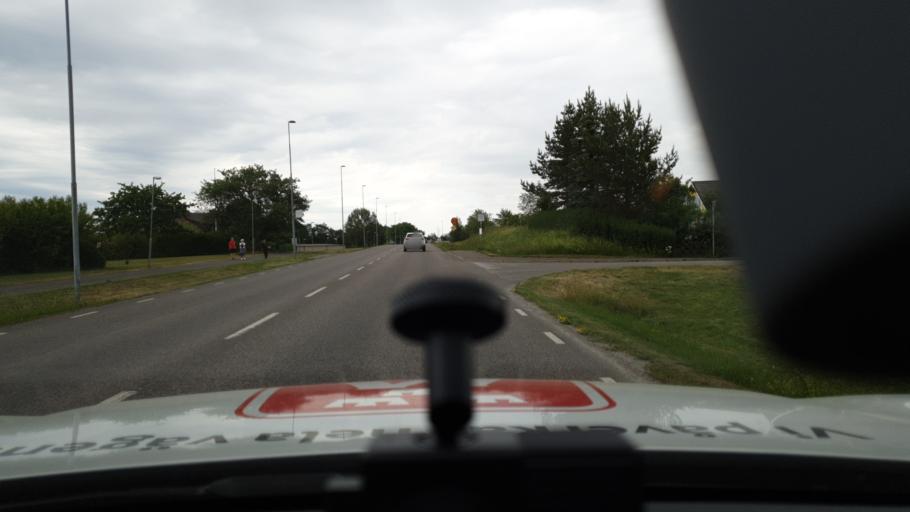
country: SE
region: Vaestra Goetaland
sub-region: Falkopings Kommun
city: Falkoeping
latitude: 58.1572
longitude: 13.5628
